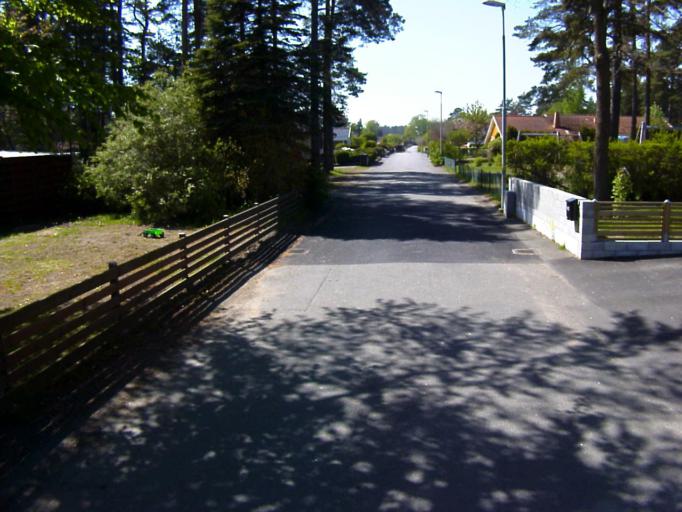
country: SE
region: Skane
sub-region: Kristianstads Kommun
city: Degeberga
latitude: 55.9017
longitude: 14.0994
